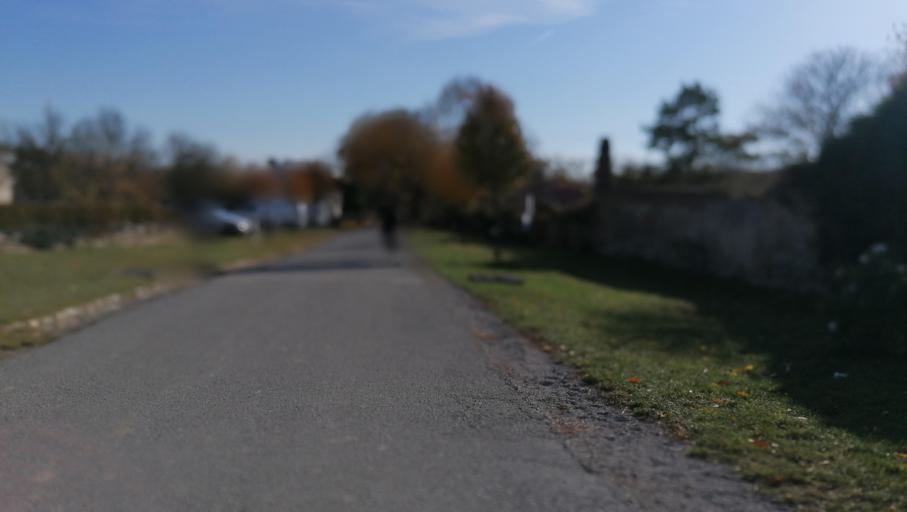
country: AT
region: Lower Austria
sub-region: Politischer Bezirk Modling
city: Gumpoldskirchen
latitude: 48.0521
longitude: 16.2932
